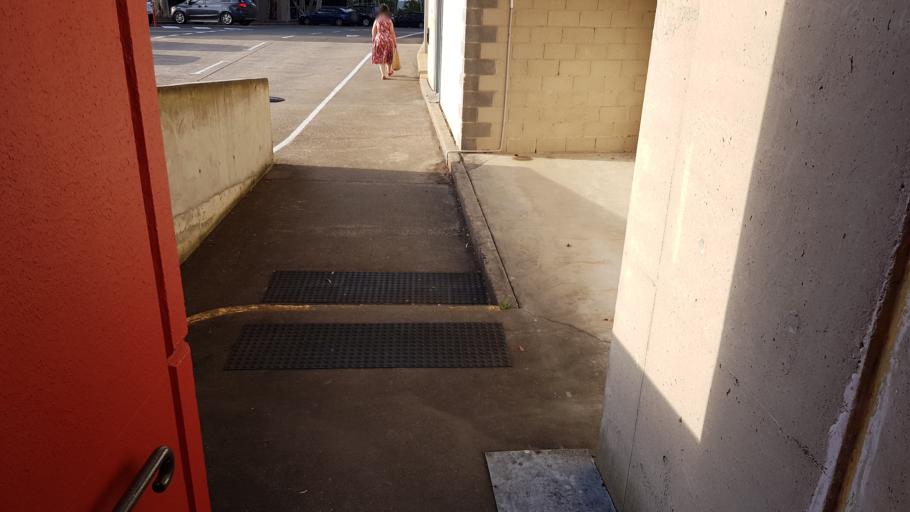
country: AU
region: New South Wales
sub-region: Warringah
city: Allambie Heights
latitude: -33.7529
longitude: 151.2485
